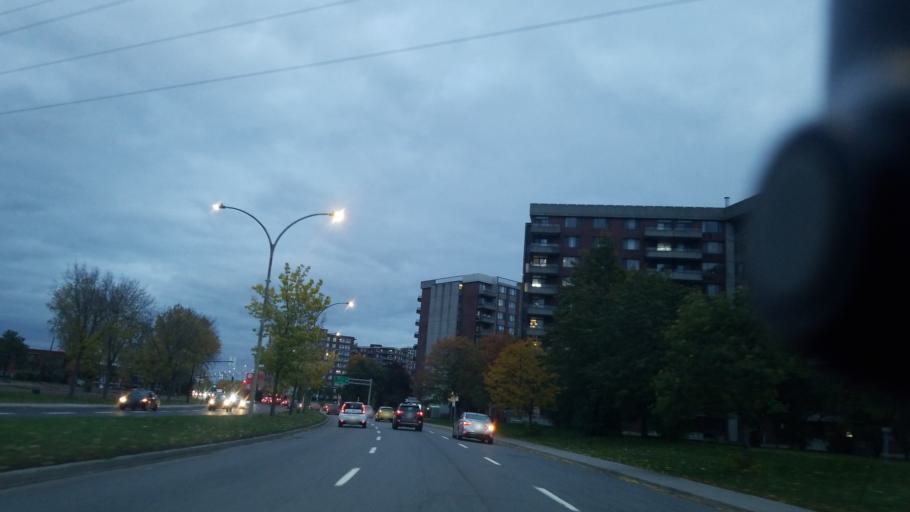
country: CA
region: Quebec
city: Mont-Royal
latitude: 45.5336
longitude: -73.6782
